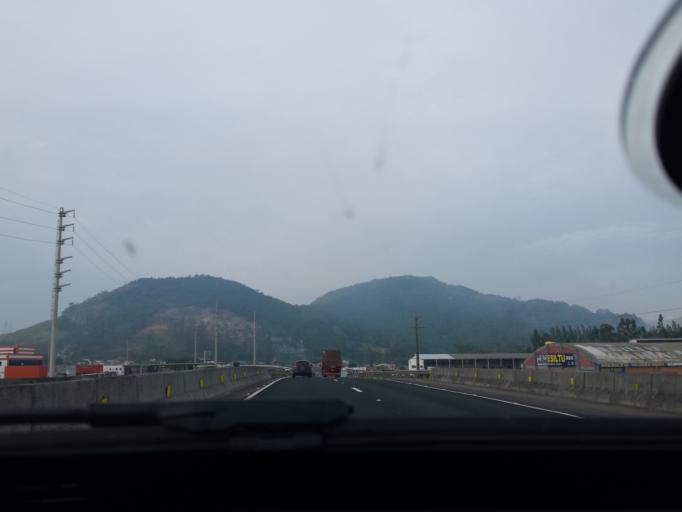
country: BR
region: Santa Catarina
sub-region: Tubarao
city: Tubarao
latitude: -28.4763
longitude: -49.0298
